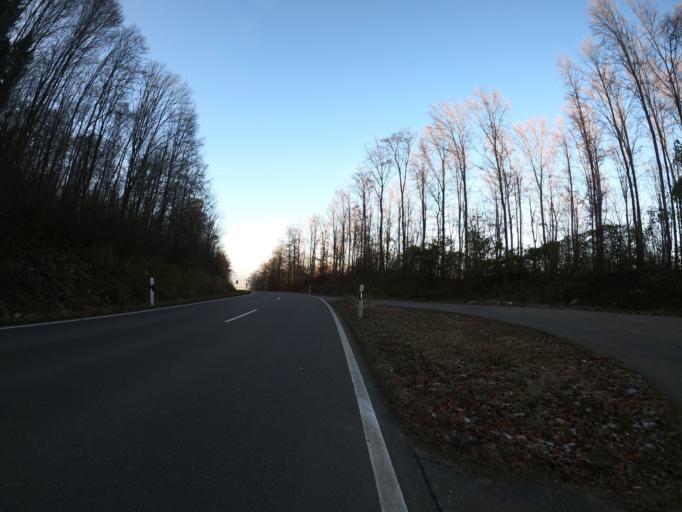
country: DE
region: Baden-Wuerttemberg
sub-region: Regierungsbezirk Stuttgart
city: Gammelshausen
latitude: 48.6317
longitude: 9.6627
